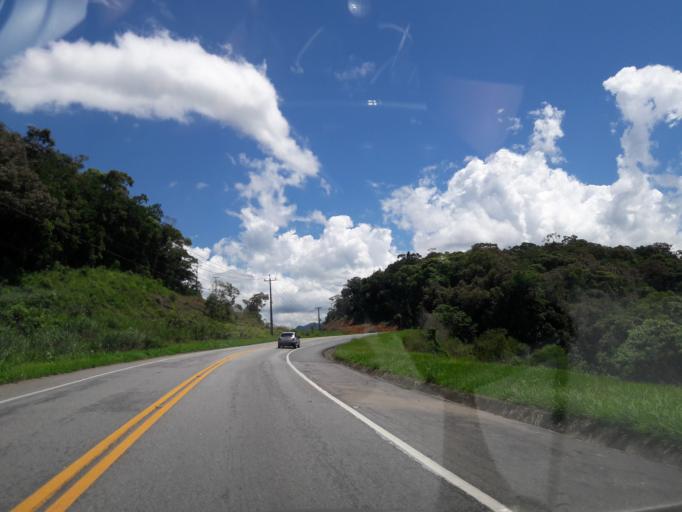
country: BR
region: Parana
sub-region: Antonina
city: Antonina
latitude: -25.4572
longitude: -48.8135
